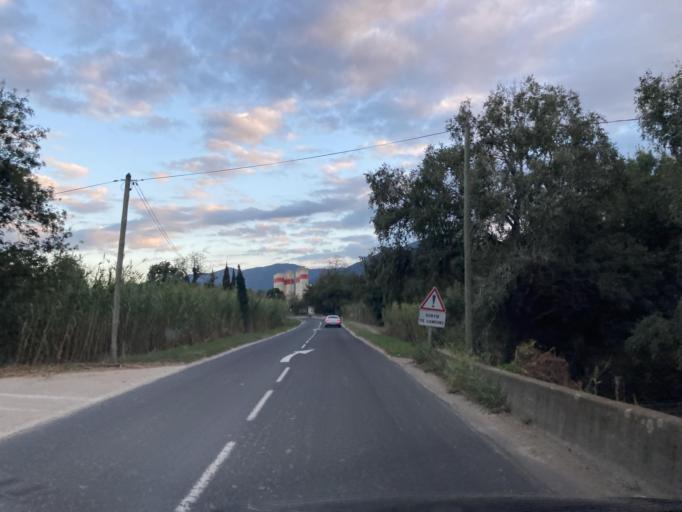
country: FR
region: Languedoc-Roussillon
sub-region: Departement des Pyrenees-Orientales
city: Sant Genis de Fontanes
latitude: 42.5597
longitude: 2.9047
